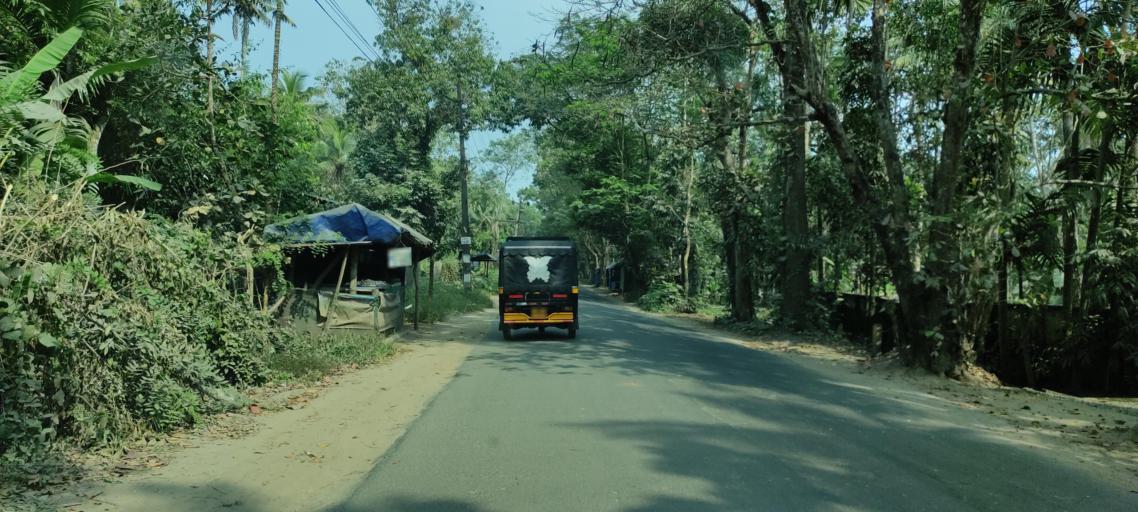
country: IN
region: Kerala
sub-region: Alappuzha
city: Shertallai
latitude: 9.6717
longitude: 76.4149
